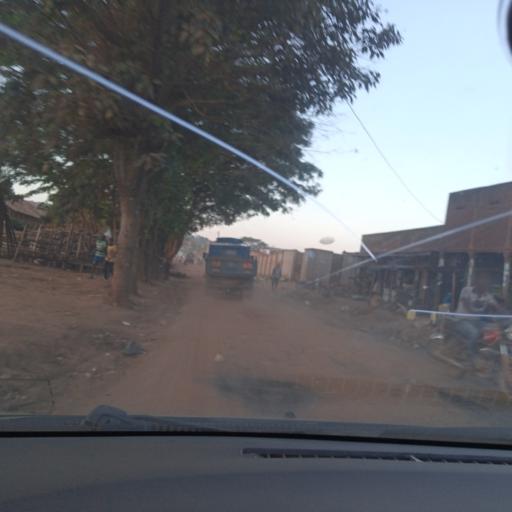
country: UG
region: Central Region
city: Masaka
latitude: -0.3226
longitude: 31.7627
